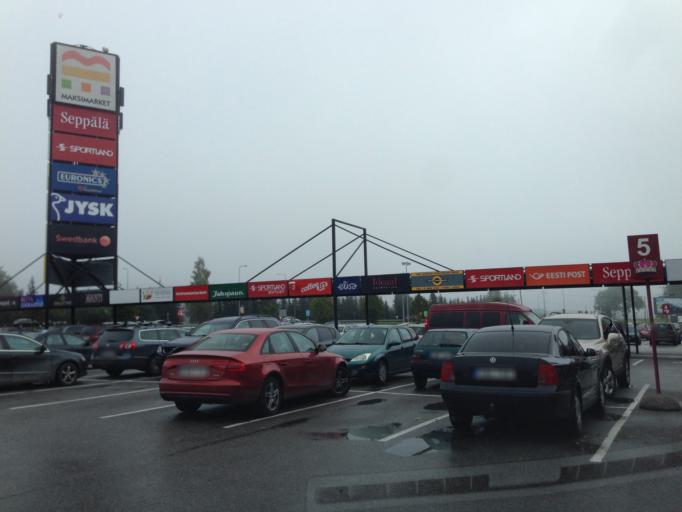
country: EE
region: Tartu
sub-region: Tartu linn
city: Tartu
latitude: 58.3587
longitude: 26.6783
